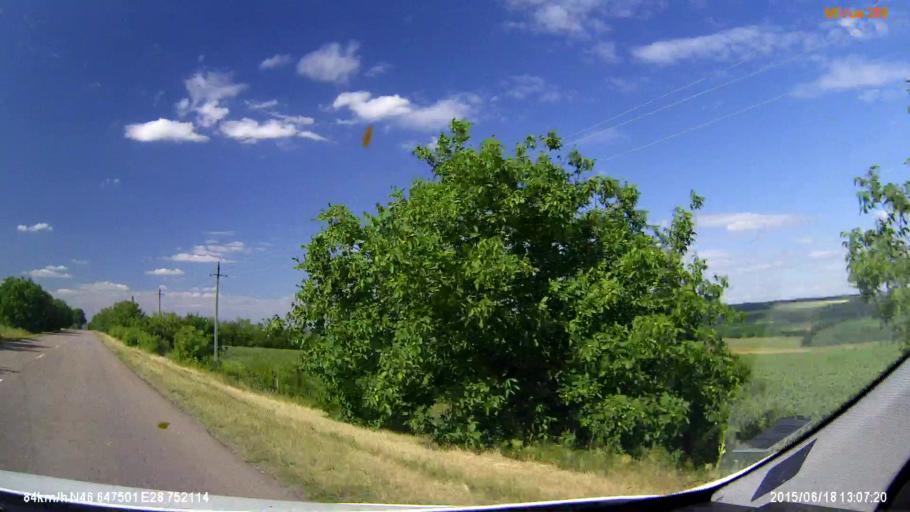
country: MD
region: Cimislia
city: Cimislia
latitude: 46.6473
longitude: 28.7521
